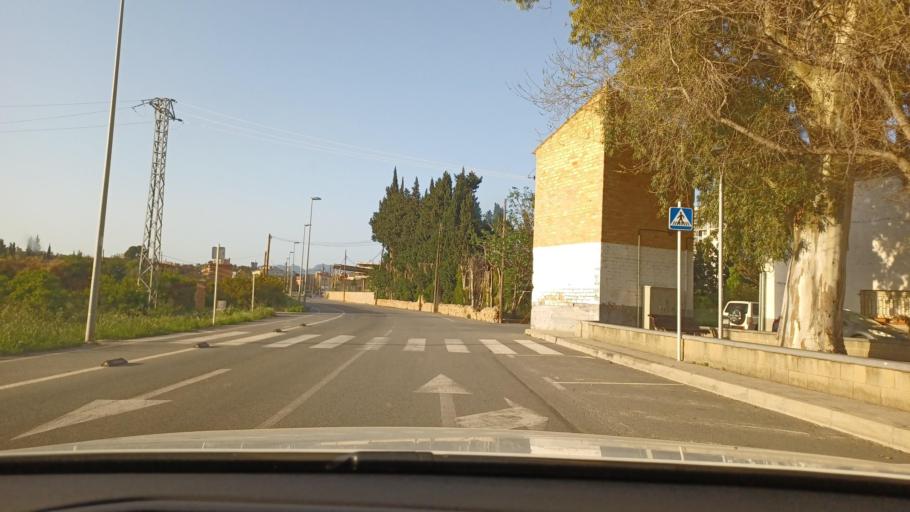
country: ES
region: Catalonia
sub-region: Provincia de Tarragona
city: Tortosa
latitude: 40.7995
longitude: 0.5178
